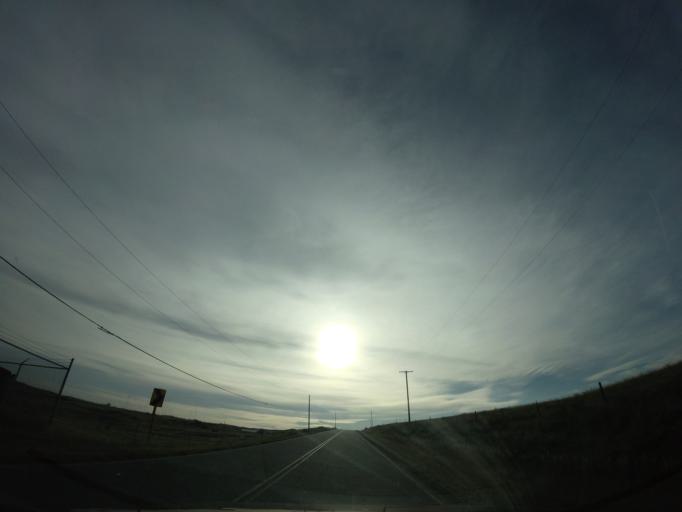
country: US
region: Montana
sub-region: Yellowstone County
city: Billings
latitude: 45.7886
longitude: -108.4558
